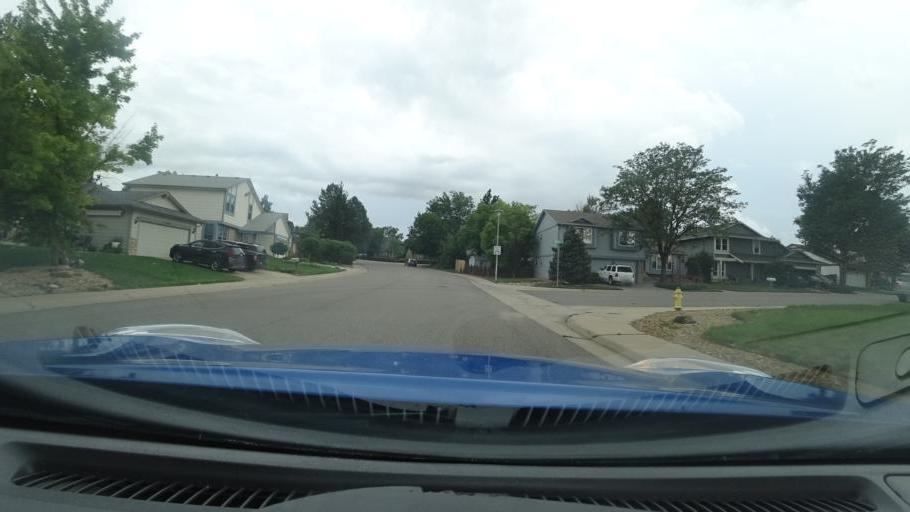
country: US
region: Colorado
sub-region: Adams County
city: Aurora
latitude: 39.7035
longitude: -104.8177
